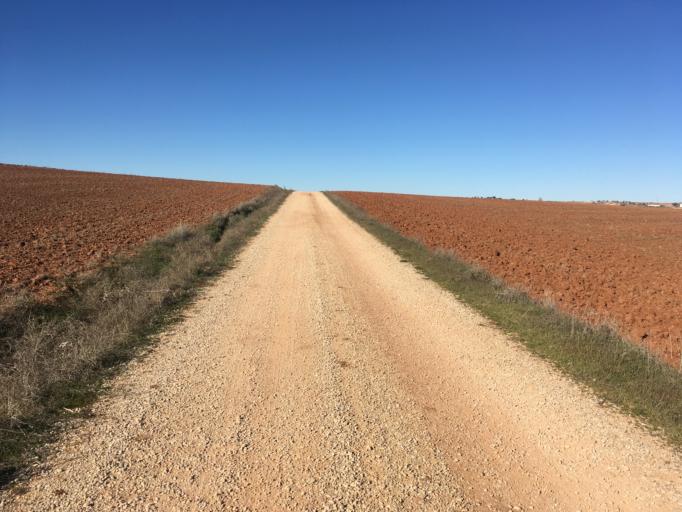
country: ES
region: Castille-La Mancha
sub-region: Provincia de Cuenca
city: Atalaya del Canavate
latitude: 39.5414
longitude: -2.2425
